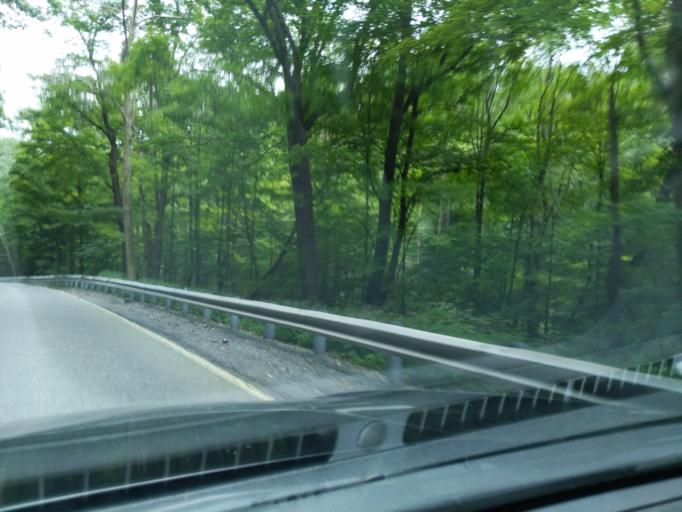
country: US
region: Pennsylvania
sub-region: Cambria County
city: Cresson
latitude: 40.3603
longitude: -78.5500
